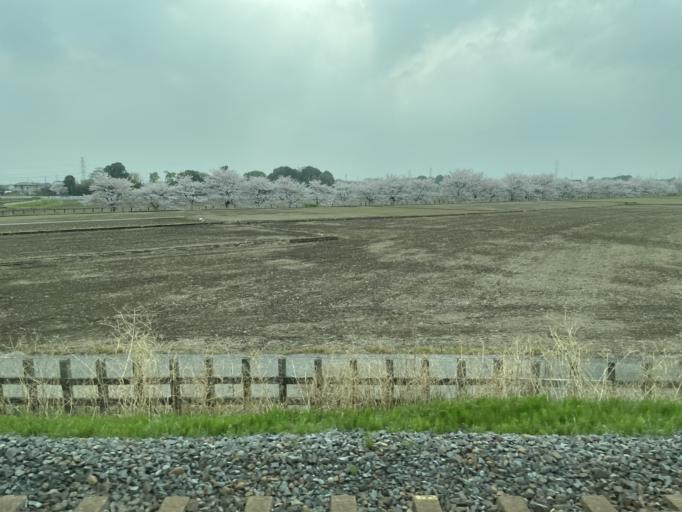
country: JP
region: Saitama
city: Sugito
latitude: 36.0114
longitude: 139.7360
